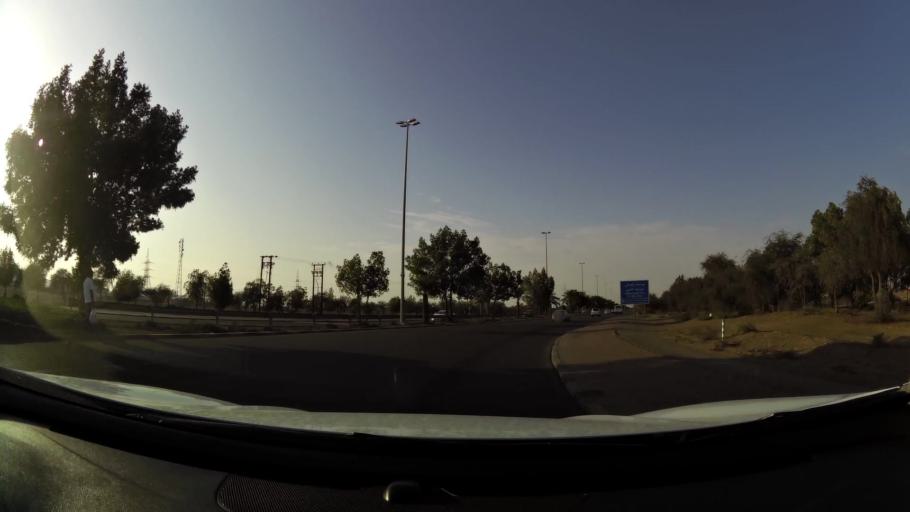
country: AE
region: Abu Dhabi
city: Al Ain
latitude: 24.1113
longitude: 55.8255
